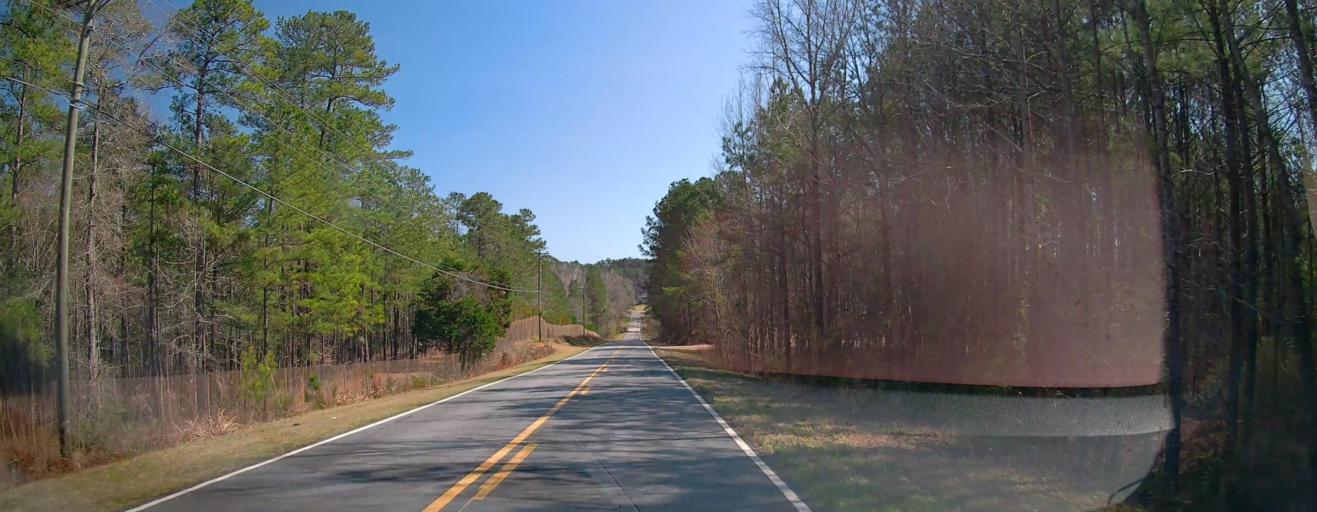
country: US
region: Georgia
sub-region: Bibb County
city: Macon
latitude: 32.8986
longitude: -83.6120
